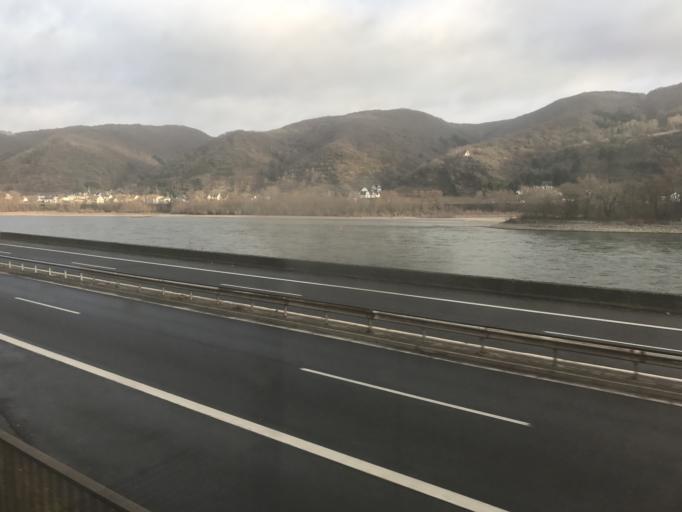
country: DE
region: Rheinland-Pfalz
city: Hammerstein
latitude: 50.4704
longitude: 7.3462
